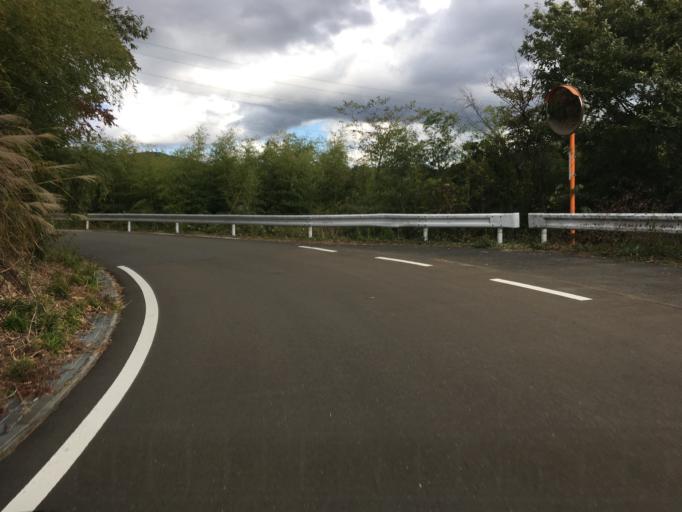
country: JP
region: Miyagi
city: Marumori
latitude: 37.7964
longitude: 140.7581
